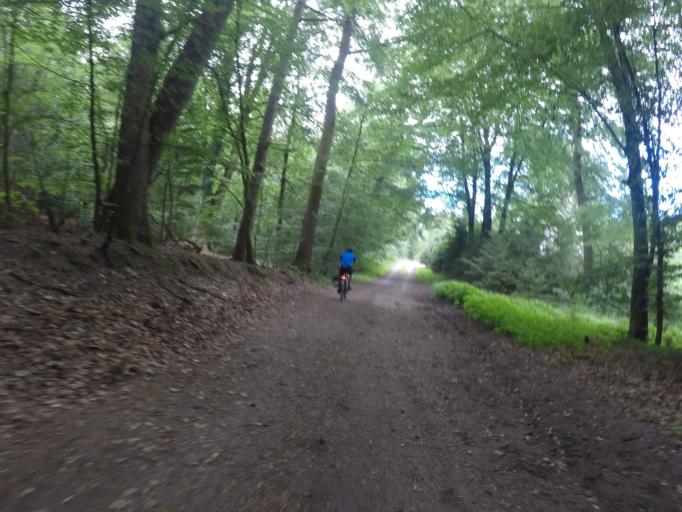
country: DE
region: Lower Saxony
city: Wingst
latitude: 53.7358
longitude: 9.0729
